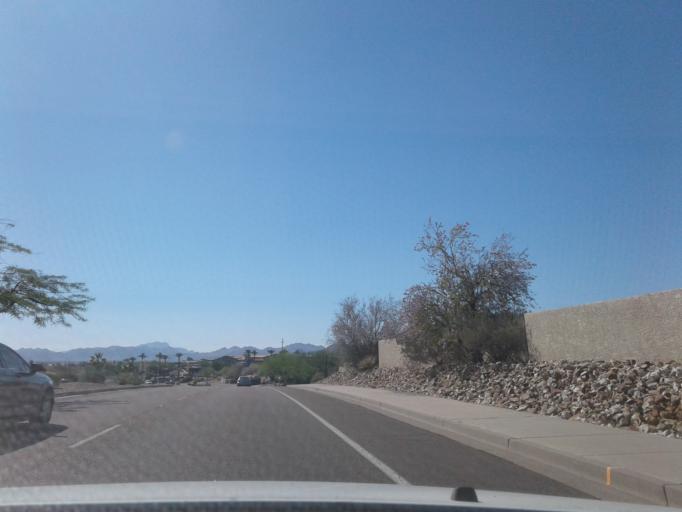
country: US
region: Arizona
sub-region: Maricopa County
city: Fountain Hills
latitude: 33.6129
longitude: -111.7316
